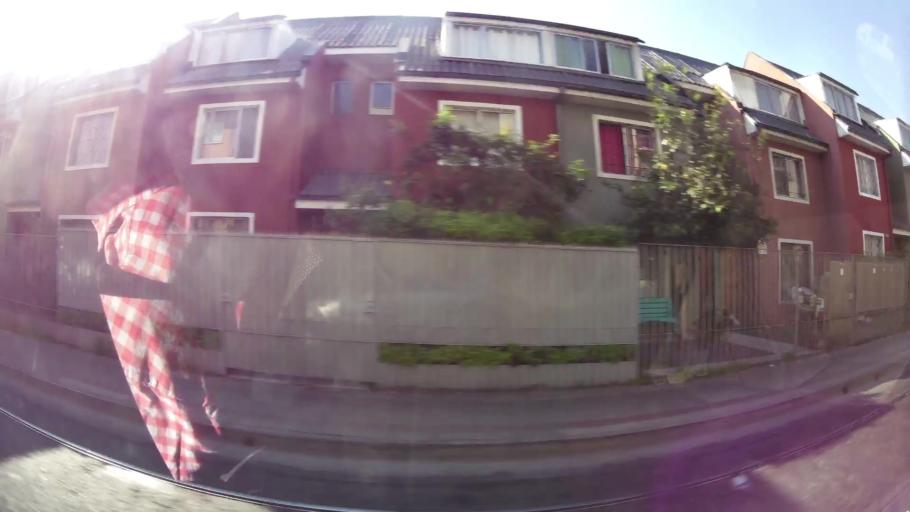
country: CL
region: Santiago Metropolitan
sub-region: Provincia de Santiago
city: Santiago
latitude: -33.4394
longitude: -70.6709
